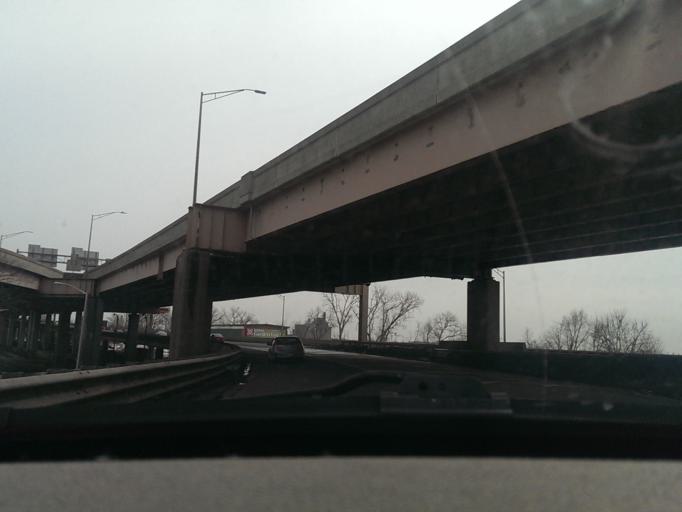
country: US
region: Massachusetts
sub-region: Hampden County
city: Springfield
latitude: 42.1063
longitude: -72.6009
